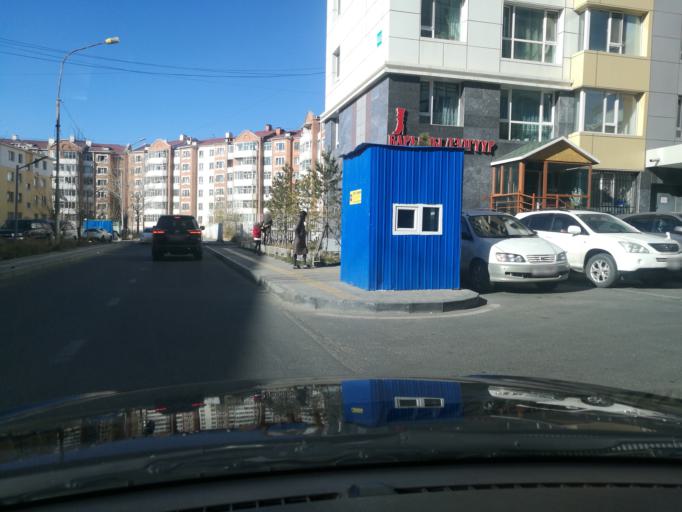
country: MN
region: Ulaanbaatar
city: Ulaanbaatar
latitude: 47.9047
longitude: 106.9102
